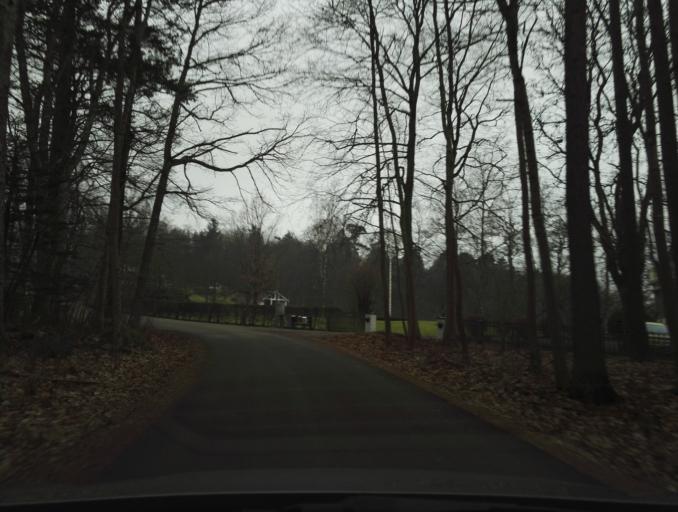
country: SE
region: Kronoberg
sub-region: Vaxjo Kommun
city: Vaexjoe
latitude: 56.9413
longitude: 14.8010
